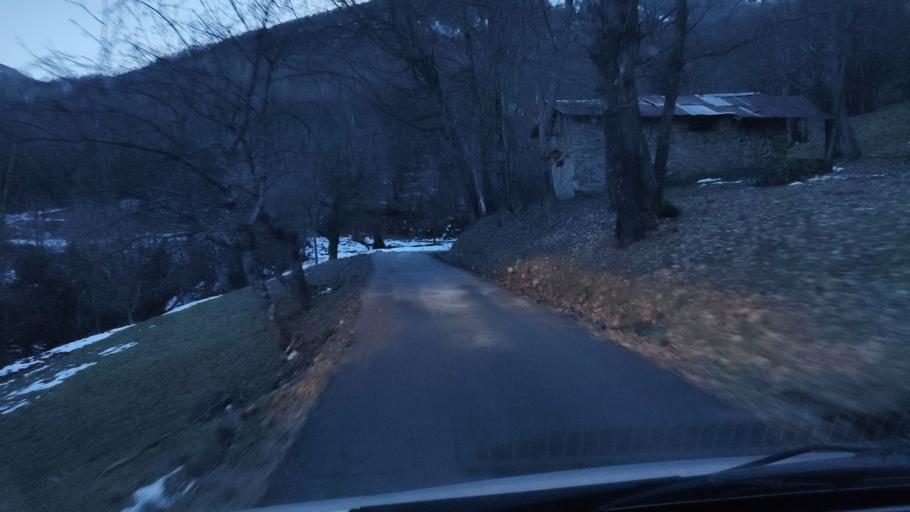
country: IT
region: Piedmont
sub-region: Provincia di Cuneo
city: Viola
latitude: 44.2789
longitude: 7.9635
